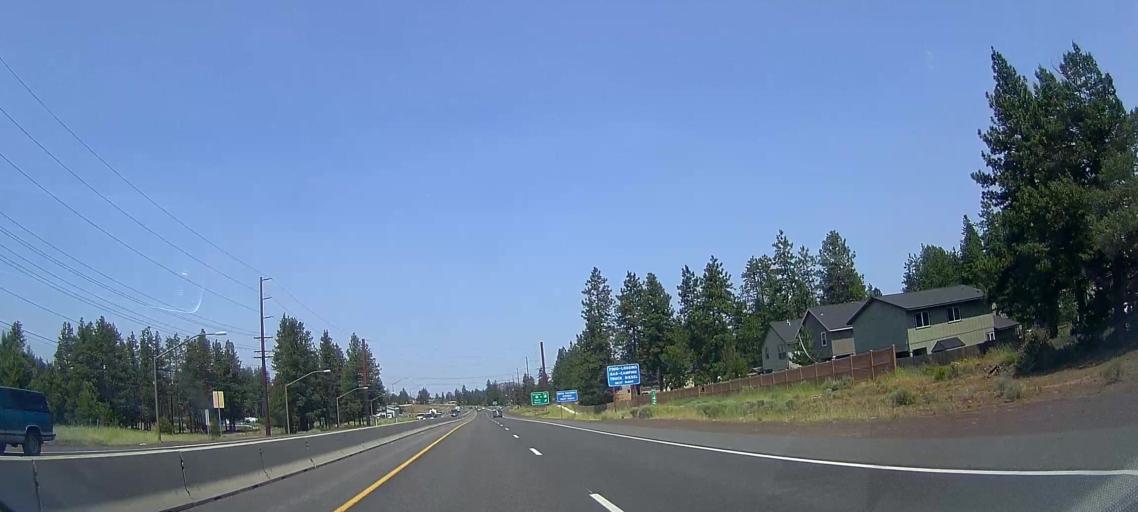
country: US
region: Oregon
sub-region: Deschutes County
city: Deschutes River Woods
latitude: 44.0107
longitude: -121.3219
